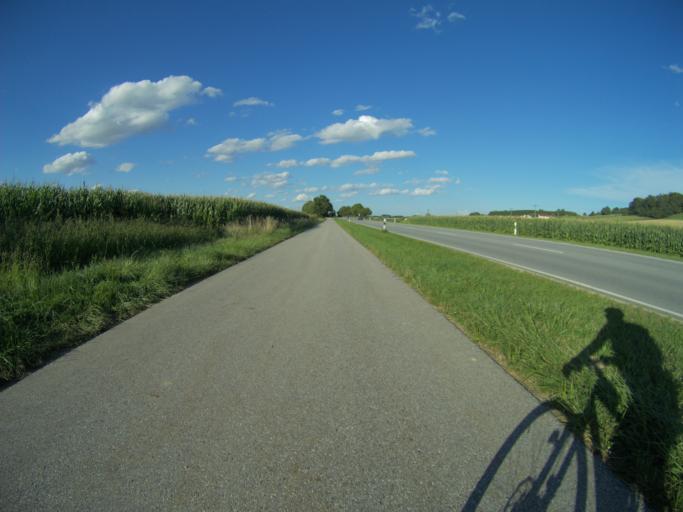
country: DE
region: Bavaria
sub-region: Upper Bavaria
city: Marzling
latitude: 48.4219
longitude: 11.8203
